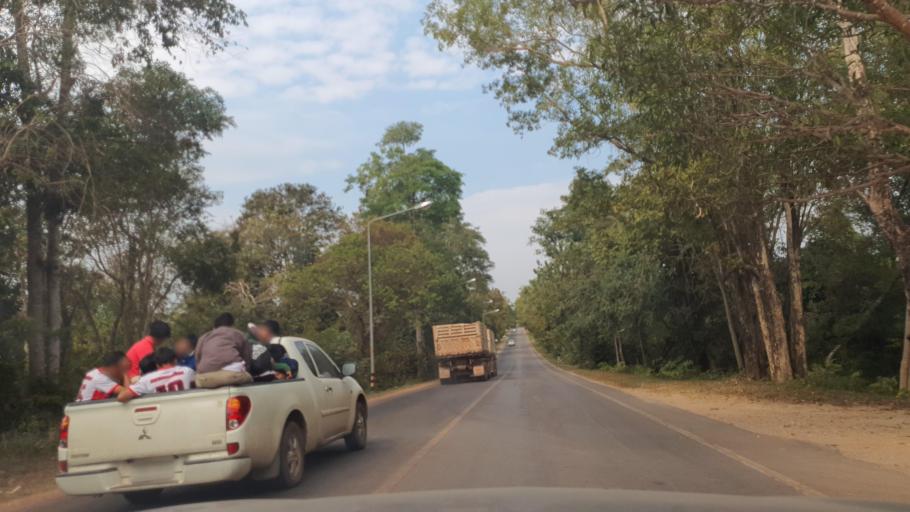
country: TH
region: Changwat Bueng Kan
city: Si Wilai
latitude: 18.2812
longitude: 103.8287
